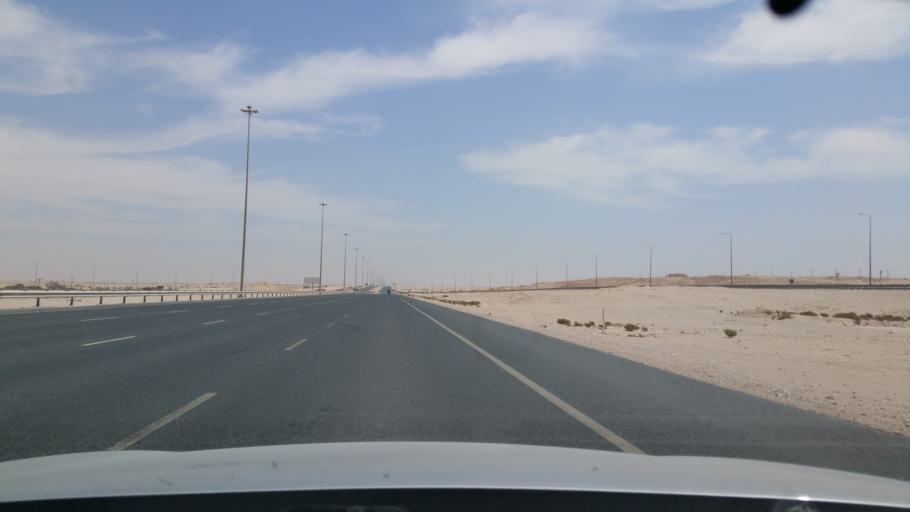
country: QA
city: Umm Bab
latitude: 25.0087
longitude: 51.0461
